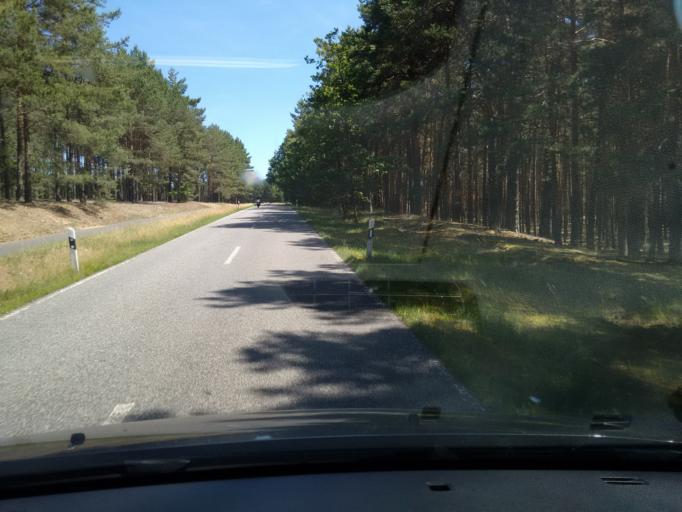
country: DE
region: Brandenburg
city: Mixdorf
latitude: 52.1859
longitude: 14.4479
